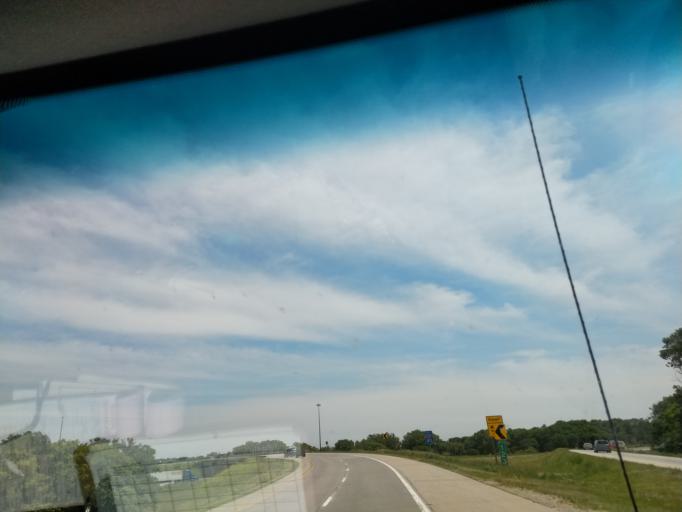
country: US
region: Iowa
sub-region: Polk County
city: Clive
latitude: 41.5902
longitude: -93.7800
